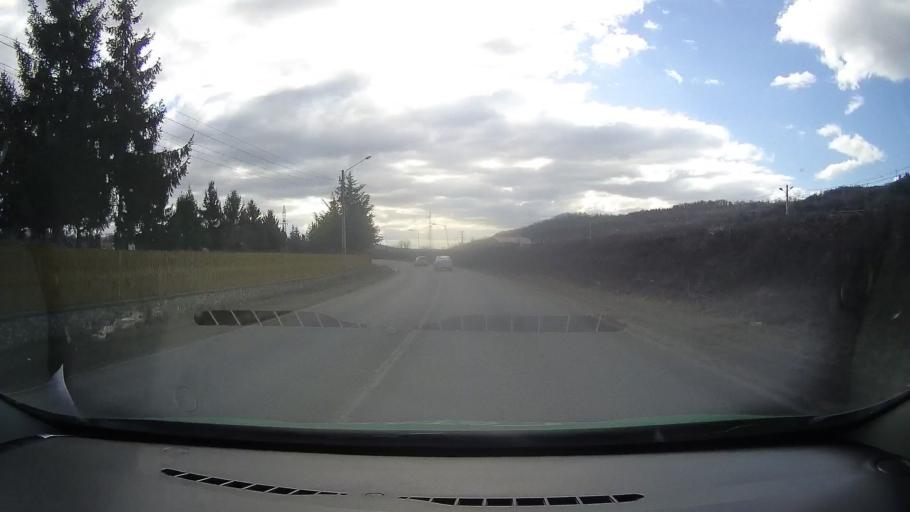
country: RO
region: Dambovita
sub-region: Oras Pucioasa
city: Pucioasa
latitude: 45.0850
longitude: 25.4215
